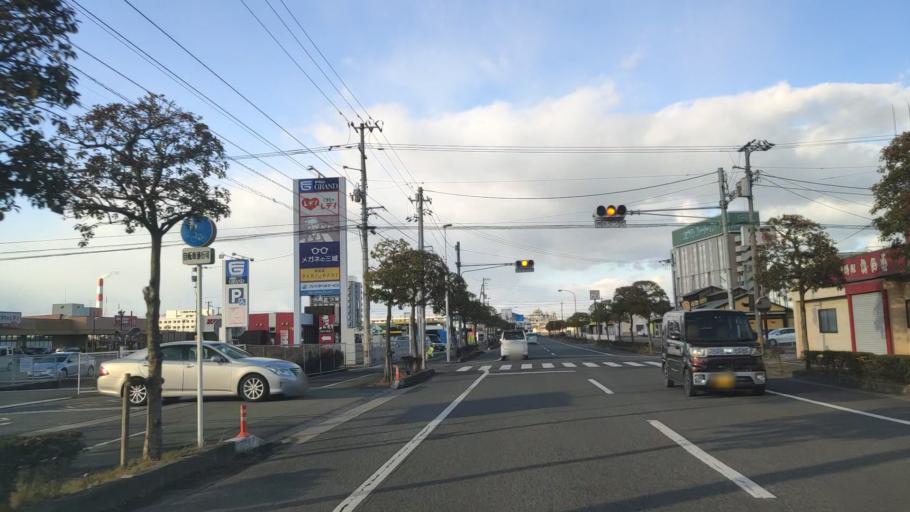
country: JP
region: Ehime
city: Saijo
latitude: 33.9258
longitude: 133.1837
